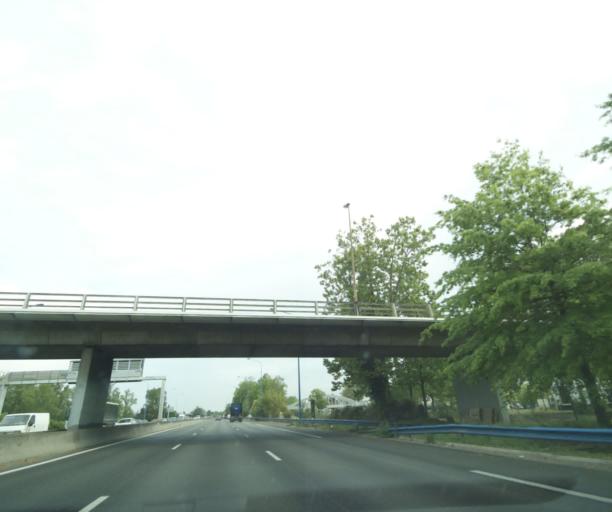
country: FR
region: Midi-Pyrenees
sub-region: Departement de la Haute-Garonne
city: Blagnac
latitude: 43.6337
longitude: 1.4209
